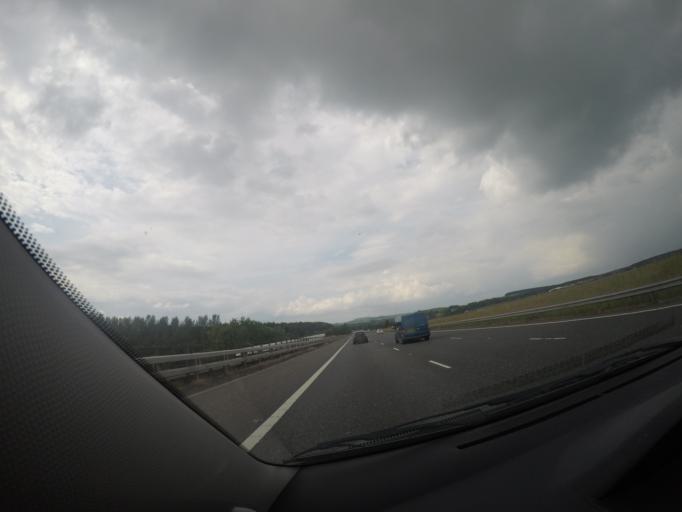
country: GB
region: Scotland
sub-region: Dumfries and Galloway
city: Lockerbie
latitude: 55.0845
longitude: -3.3176
